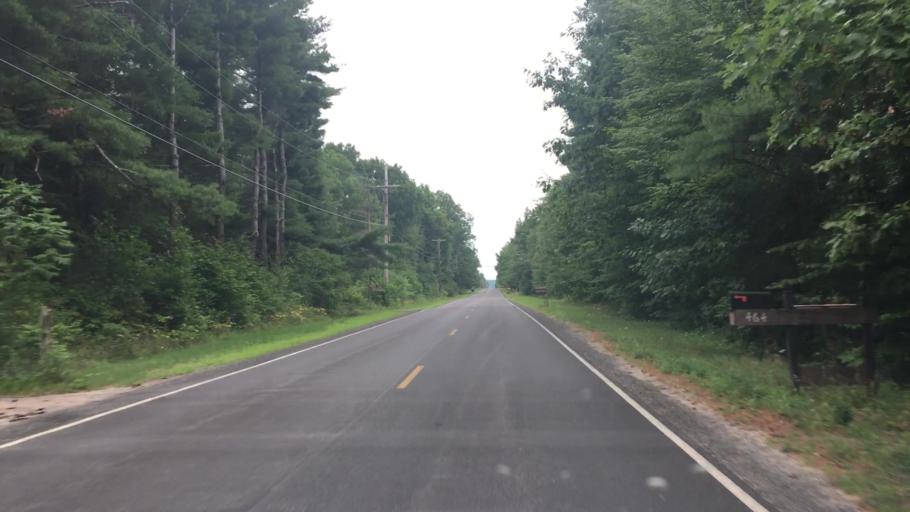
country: US
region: New York
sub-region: Clinton County
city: Peru
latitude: 44.5940
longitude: -73.6269
